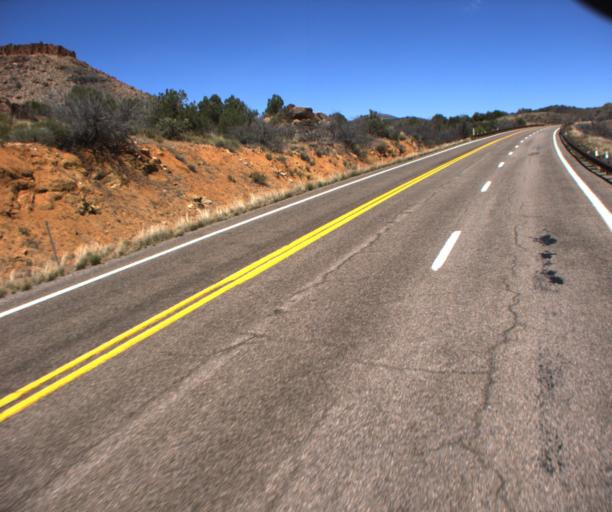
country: US
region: Arizona
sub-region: Mohave County
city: Peach Springs
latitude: 35.4304
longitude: -113.6492
